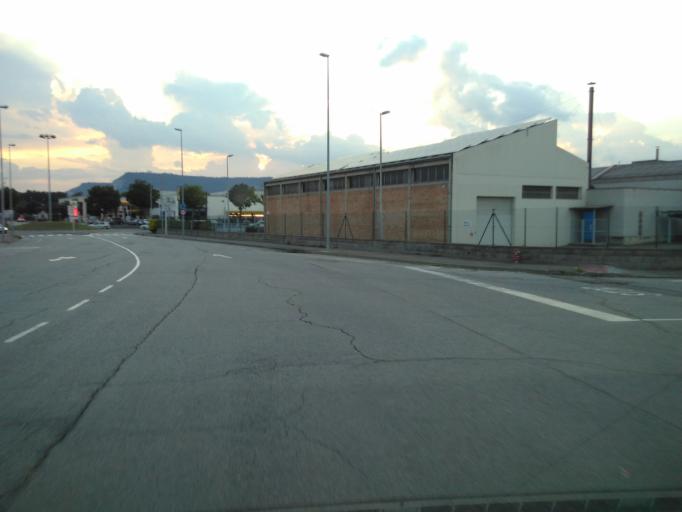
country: ES
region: Catalonia
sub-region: Provincia de Barcelona
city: Vic
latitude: 41.9411
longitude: 2.2551
